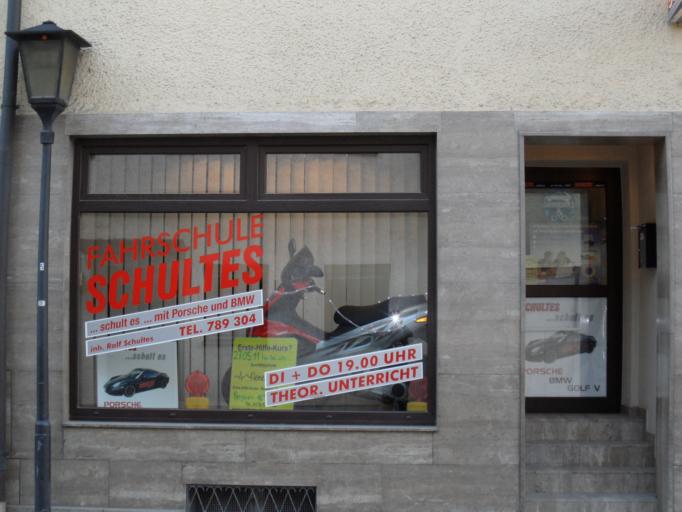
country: DE
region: Bavaria
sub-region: Upper Bavaria
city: Pfaffenhofen an der Ilm
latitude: 48.5329
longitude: 11.5091
